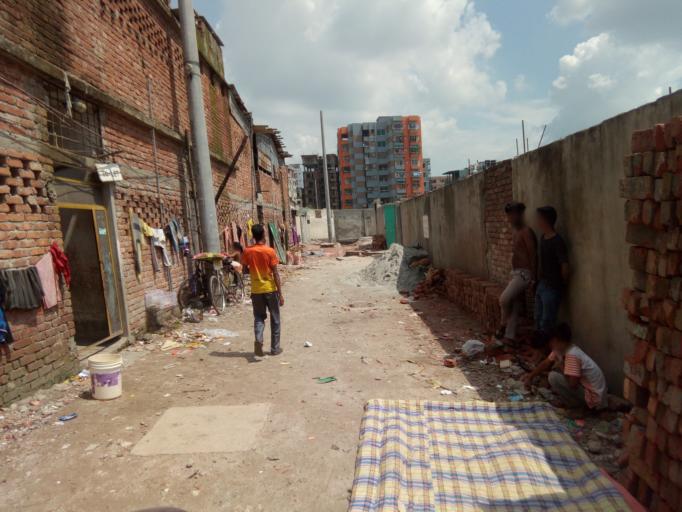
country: BD
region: Dhaka
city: Azimpur
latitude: 23.7433
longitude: 90.3620
